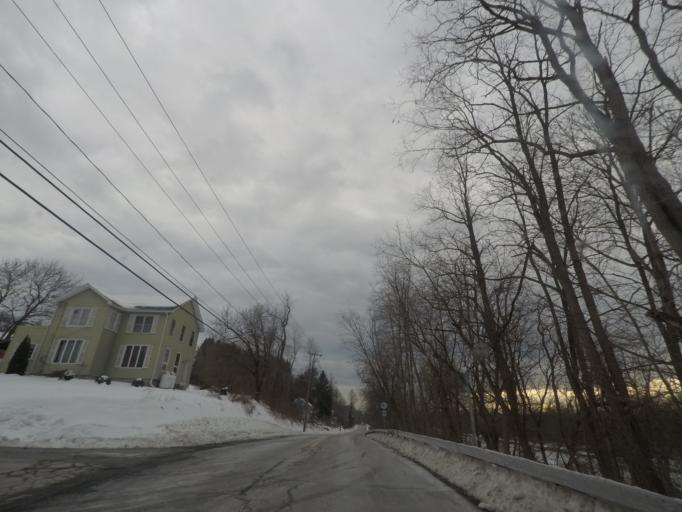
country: US
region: New York
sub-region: Rensselaer County
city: Castleton-on-Hudson
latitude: 42.4959
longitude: -73.7675
